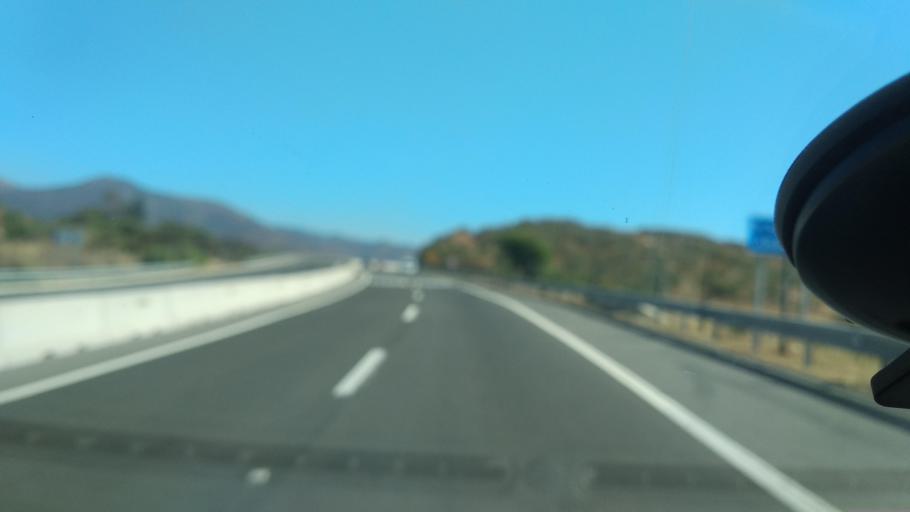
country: CL
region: Valparaiso
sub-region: Provincia de Marga Marga
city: Villa Alemana
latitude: -33.0316
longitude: -71.3200
